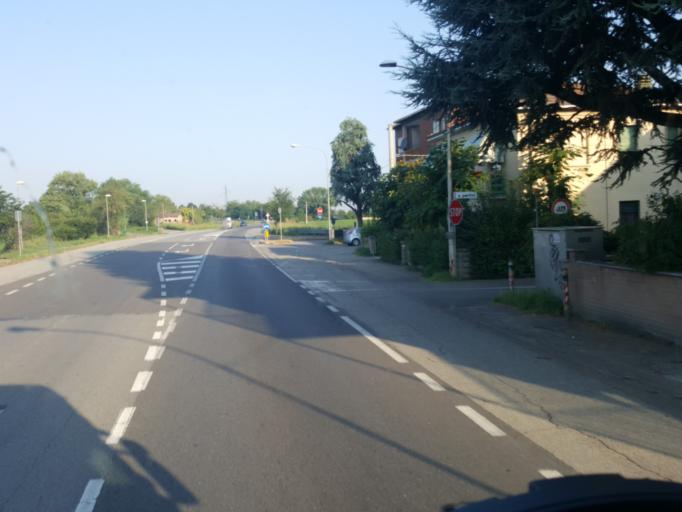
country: IT
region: Emilia-Romagna
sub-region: Provincia di Modena
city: Spilamberto
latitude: 44.5362
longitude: 11.0015
